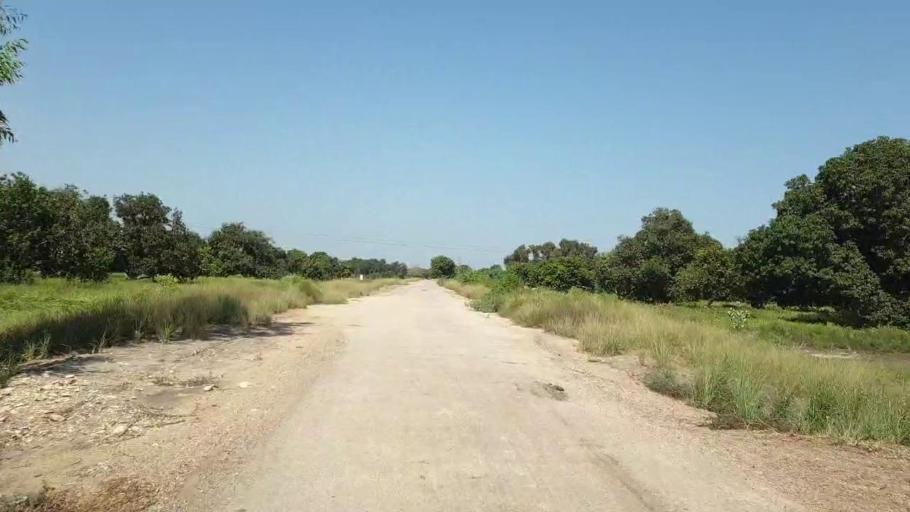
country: PK
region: Sindh
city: Tando Jam
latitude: 25.4234
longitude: 68.4587
